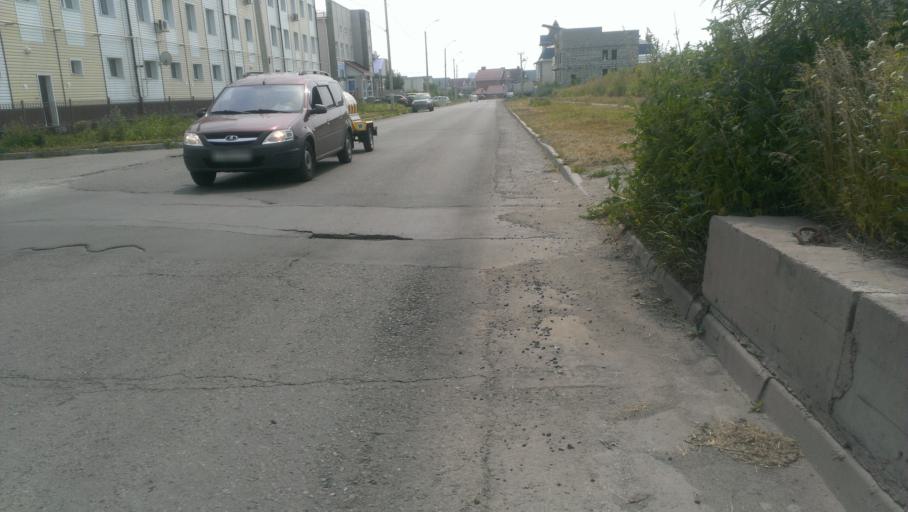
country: RU
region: Altai Krai
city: Novosilikatnyy
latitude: 53.3593
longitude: 83.6556
